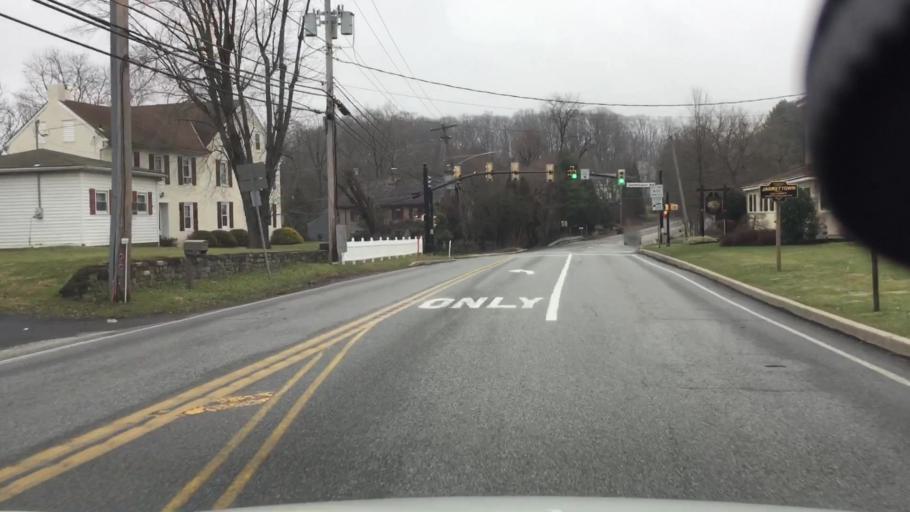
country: US
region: Pennsylvania
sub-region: Montgomery County
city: Dresher
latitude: 40.1555
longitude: -75.1760
